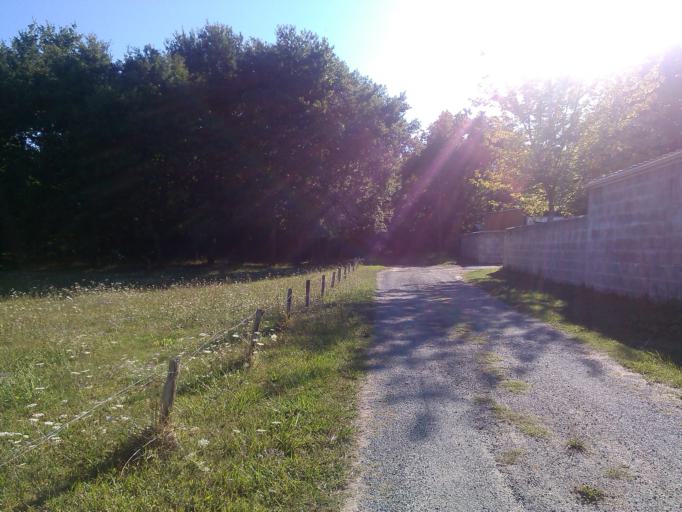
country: FR
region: Poitou-Charentes
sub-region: Departement de la Charente-Maritime
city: Chaillevette
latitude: 45.7212
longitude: -1.0615
